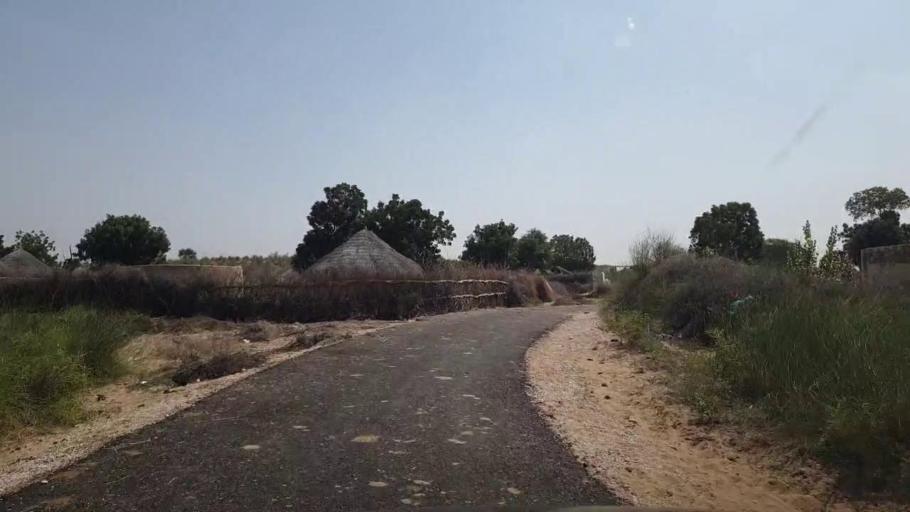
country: PK
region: Sindh
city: Islamkot
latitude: 25.0876
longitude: 70.6804
